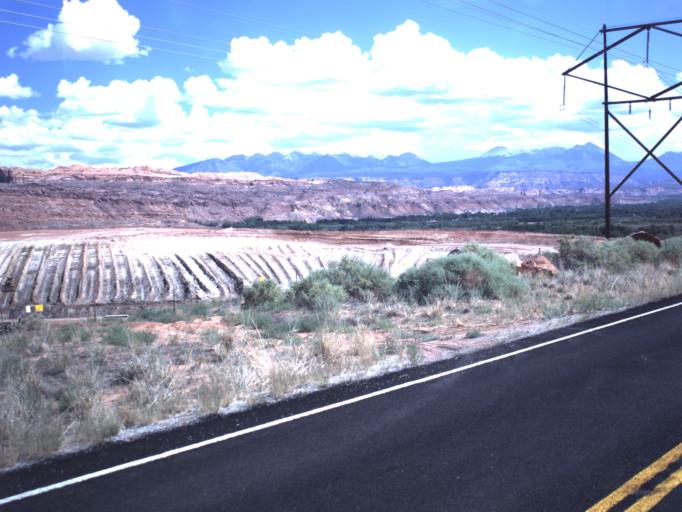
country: US
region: Utah
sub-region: Grand County
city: Moab
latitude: 38.5975
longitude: -109.6003
